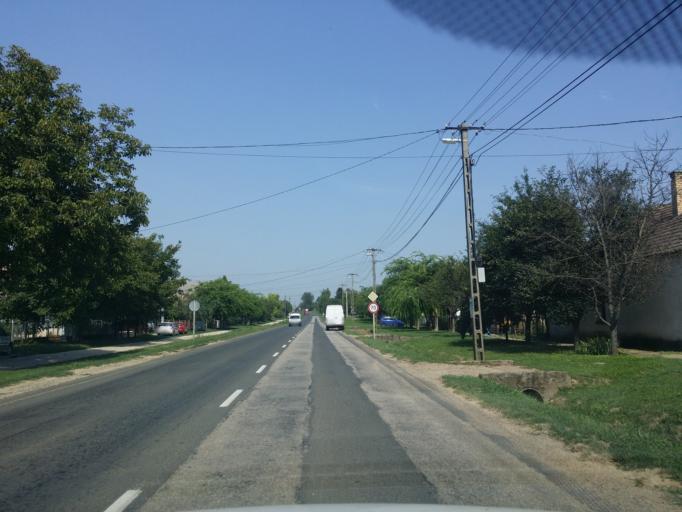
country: HU
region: Tolna
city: Pincehely
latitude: 46.7170
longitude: 18.4789
